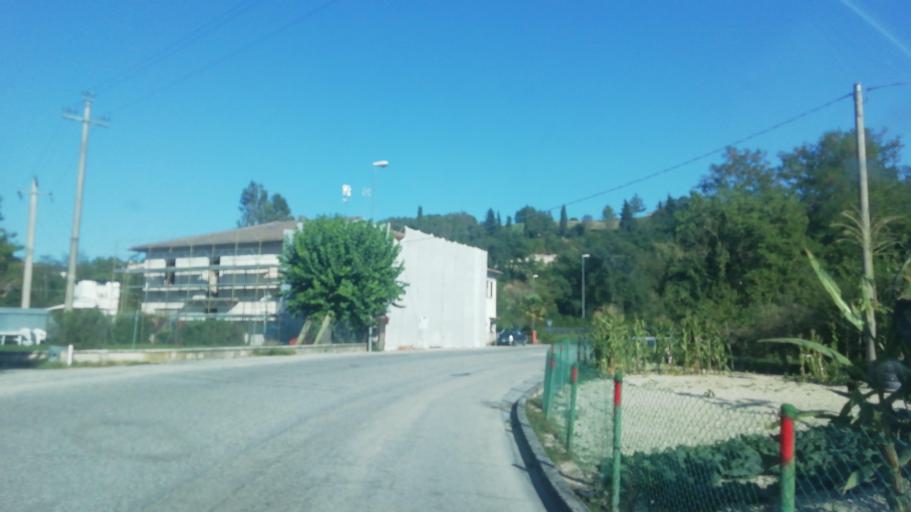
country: IT
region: The Marches
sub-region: Provincia di Pesaro e Urbino
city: Pergola
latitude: 43.5602
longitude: 12.8265
